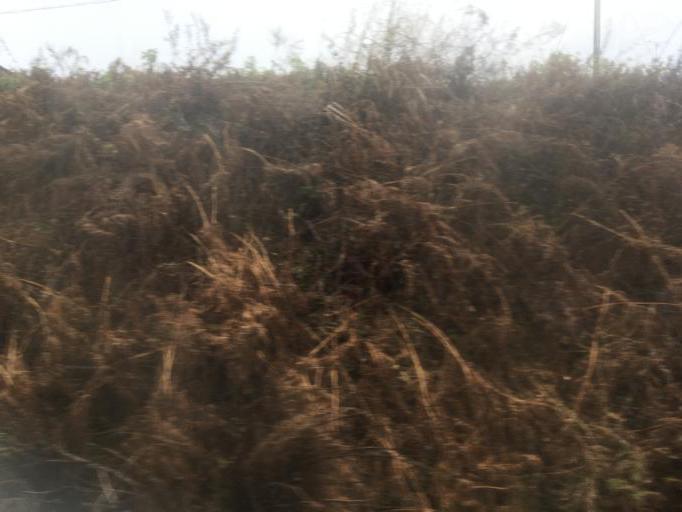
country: JP
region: Aomori
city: Goshogawara
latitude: 41.1805
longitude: 140.4753
